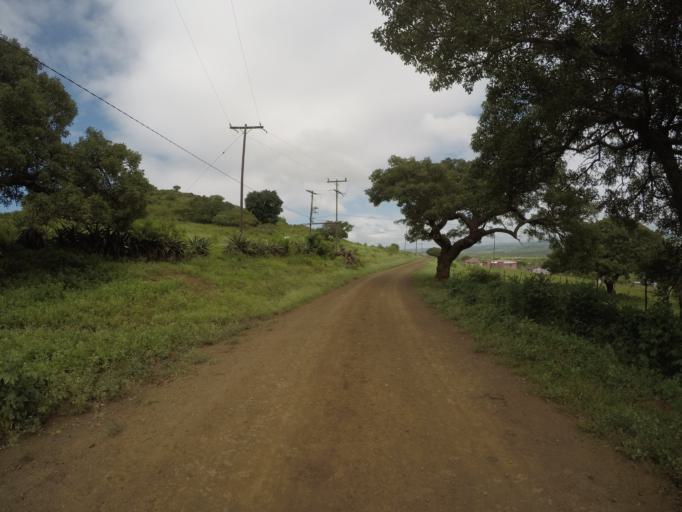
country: ZA
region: KwaZulu-Natal
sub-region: uThungulu District Municipality
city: Empangeni
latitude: -28.6280
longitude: 31.8685
